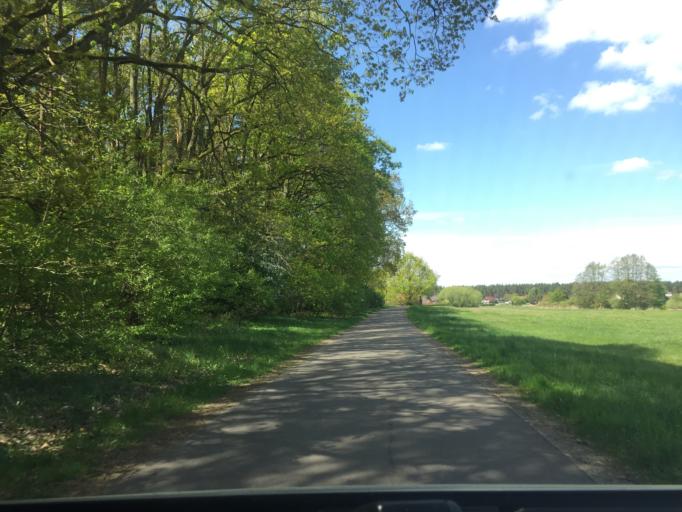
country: DE
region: Mecklenburg-Vorpommern
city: Torgelow
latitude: 53.6218
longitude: 13.9998
